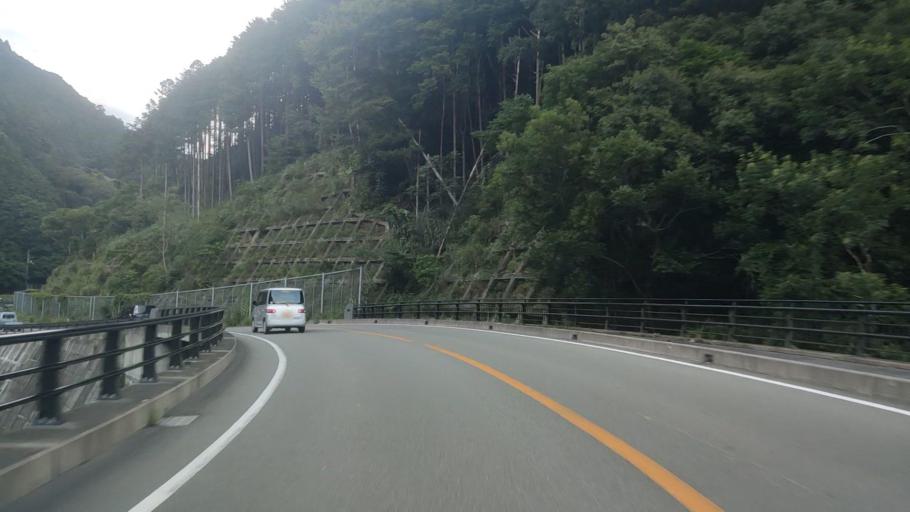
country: JP
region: Wakayama
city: Tanabe
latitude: 33.7721
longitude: 135.5008
